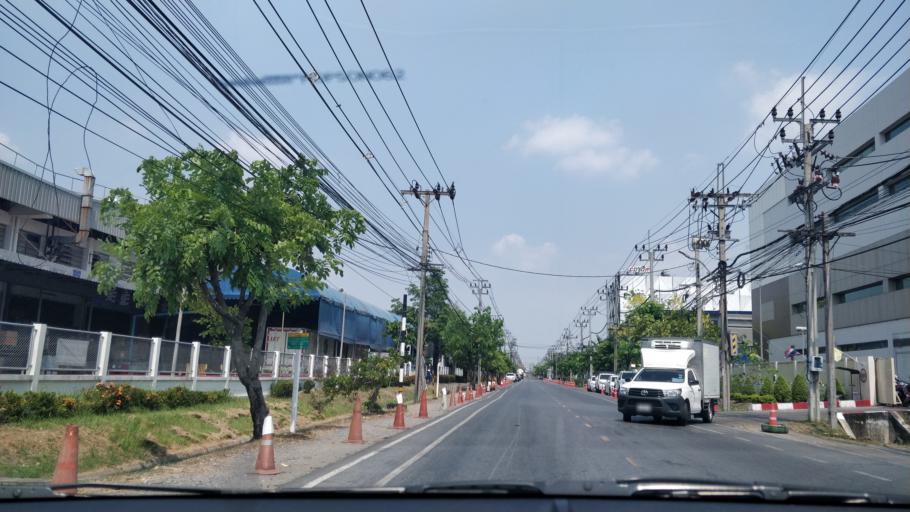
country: TH
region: Bangkok
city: Lat Krabang
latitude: 13.7713
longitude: 100.7838
